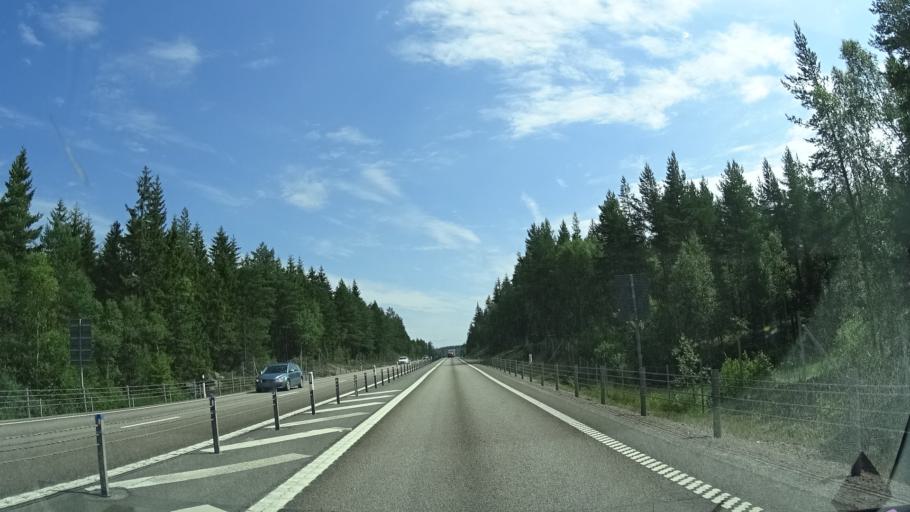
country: SE
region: Vaermland
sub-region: Kristinehamns Kommun
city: Bjorneborg
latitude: 59.3121
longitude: 14.2405
